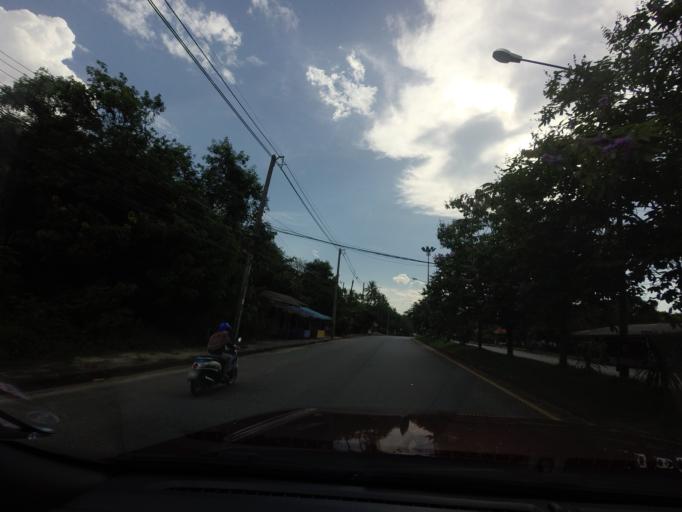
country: TH
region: Pattani
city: Khok Pho
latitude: 6.6770
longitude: 101.1426
